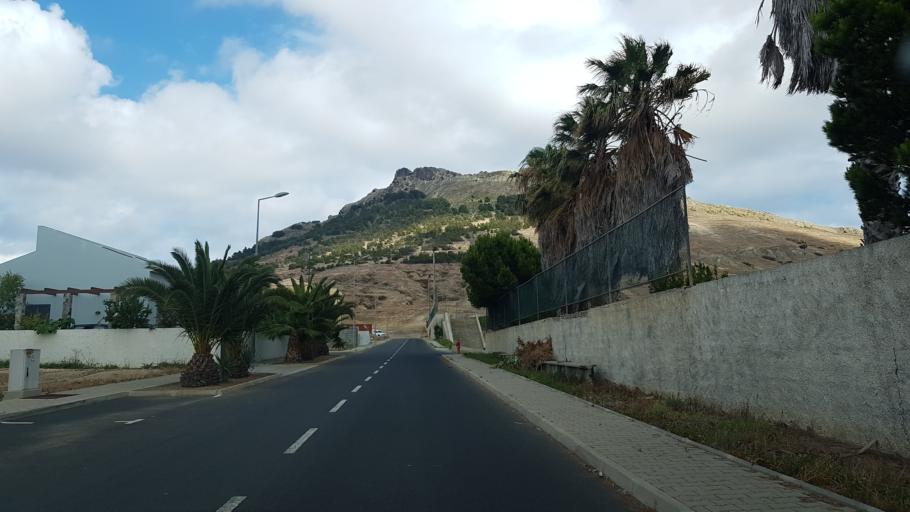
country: PT
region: Madeira
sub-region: Porto Santo
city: Vila de Porto Santo
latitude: 33.0438
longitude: -16.3592
